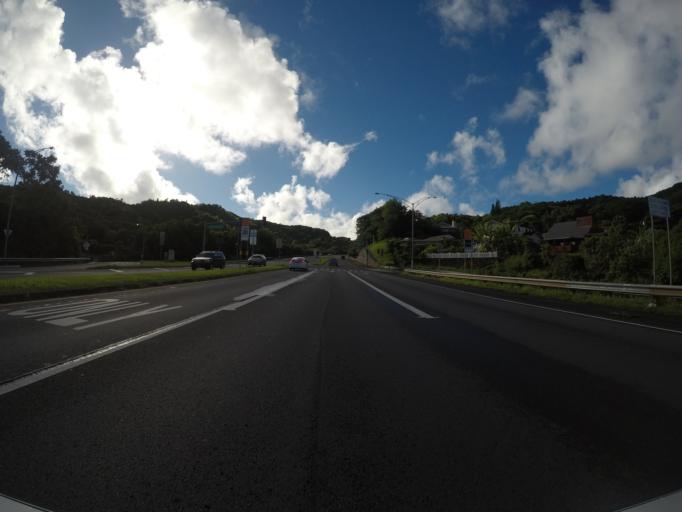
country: US
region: Hawaii
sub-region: Honolulu County
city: Kane'ohe
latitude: 21.4104
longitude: -157.7723
